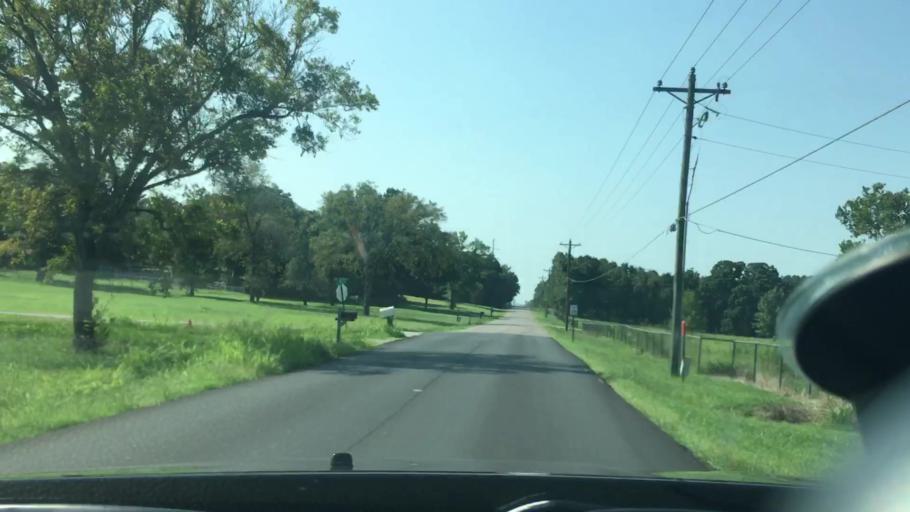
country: US
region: Oklahoma
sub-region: Bryan County
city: Durant
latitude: 34.0215
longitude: -96.4254
